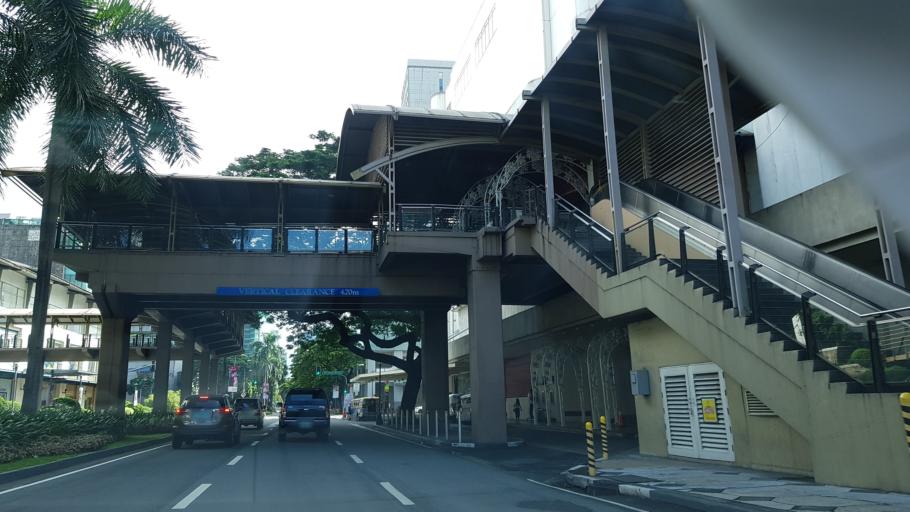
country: PH
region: Metro Manila
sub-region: Makati City
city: Makati City
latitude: 14.5518
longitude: 121.0233
